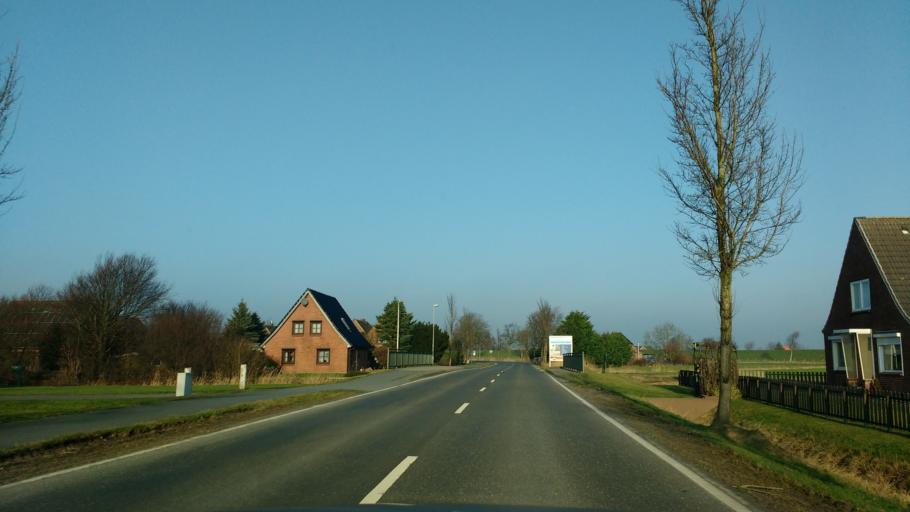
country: DE
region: Schleswig-Holstein
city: Friedrichskoog
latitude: 54.0009
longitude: 8.8874
